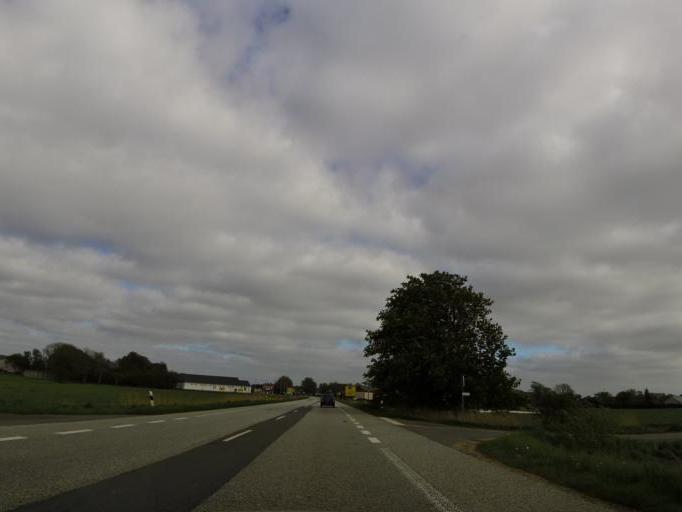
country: DE
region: Schleswig-Holstein
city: Risum-Lindholm
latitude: 54.7640
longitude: 8.8713
